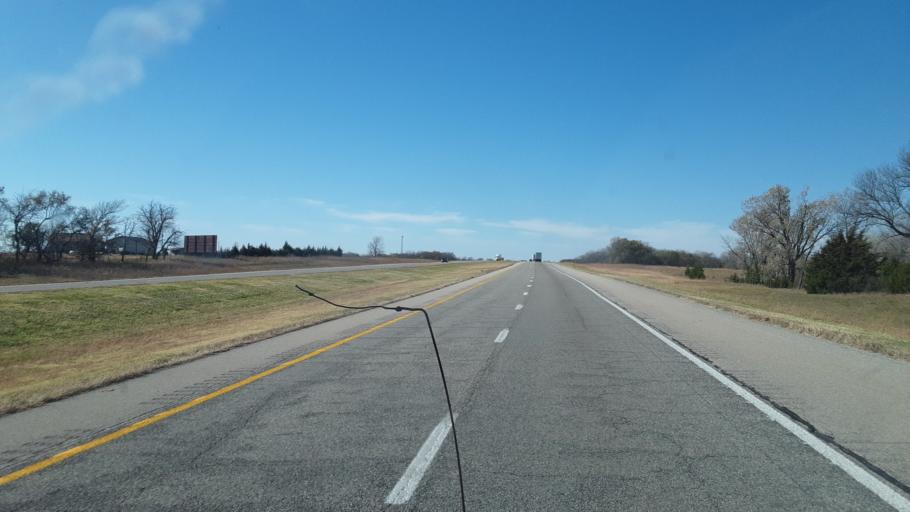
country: US
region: Kansas
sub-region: Osage County
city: Osage City
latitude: 38.4275
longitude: -95.8889
